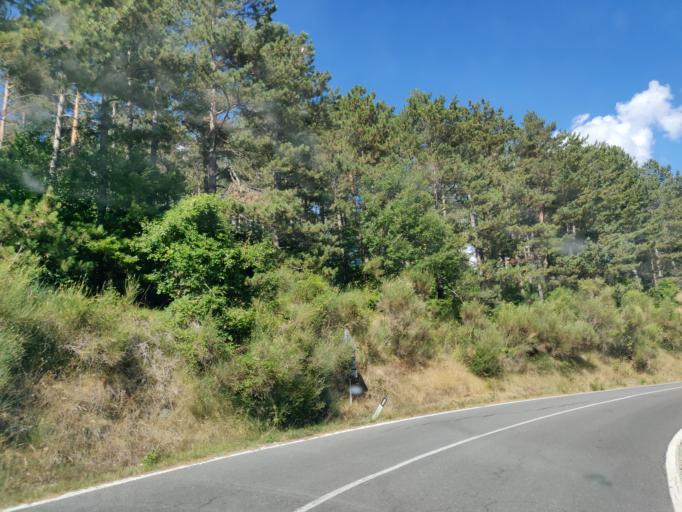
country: IT
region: Tuscany
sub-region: Provincia di Siena
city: Abbadia San Salvatore
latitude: 42.9091
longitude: 11.6696
